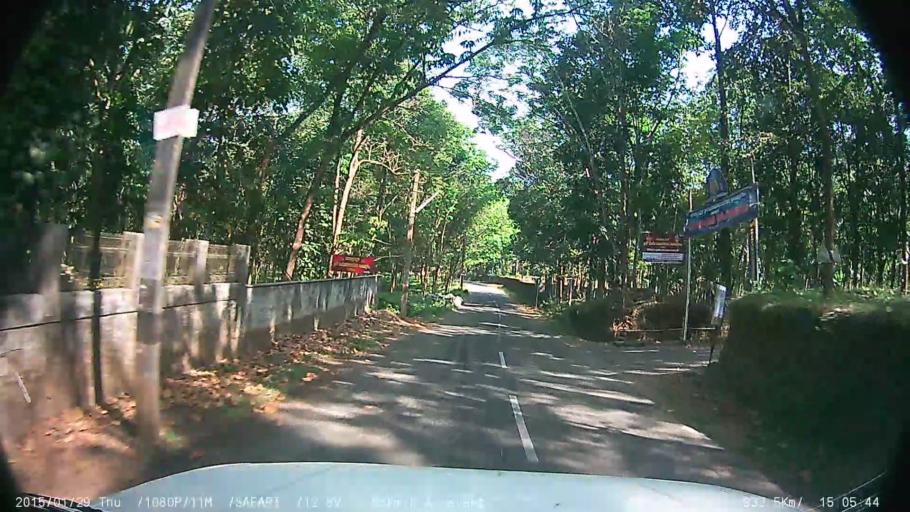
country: IN
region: Kerala
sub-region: Kottayam
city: Palackattumala
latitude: 9.7226
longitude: 76.5963
